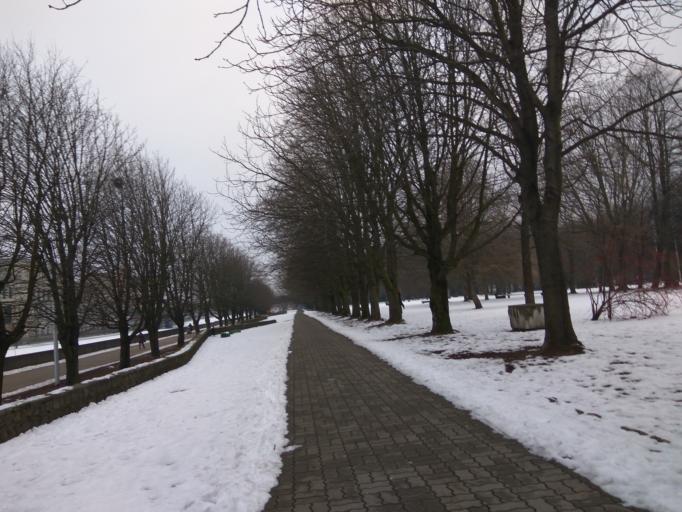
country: RU
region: Kaliningrad
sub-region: Gorod Kaliningrad
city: Kaliningrad
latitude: 54.7057
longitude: 20.5103
